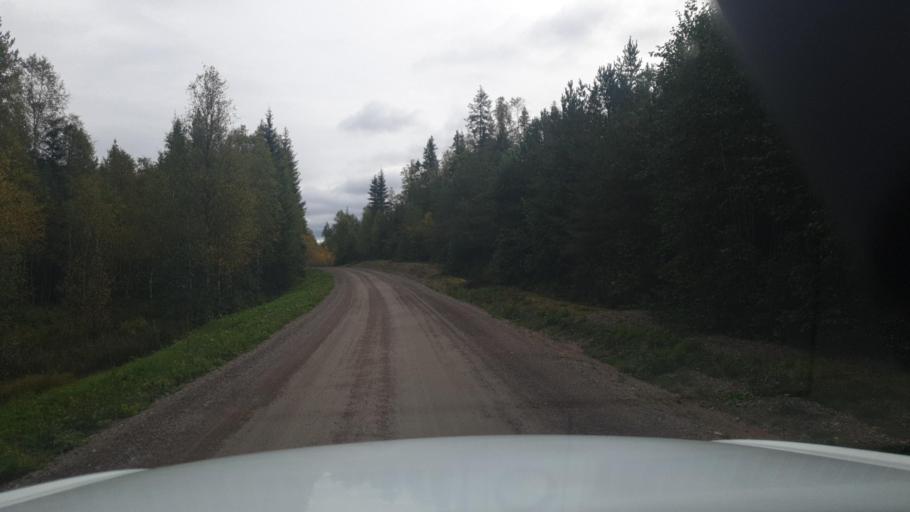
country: SE
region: Vaermland
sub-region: Eda Kommun
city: Charlottenberg
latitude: 60.0551
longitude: 12.5599
